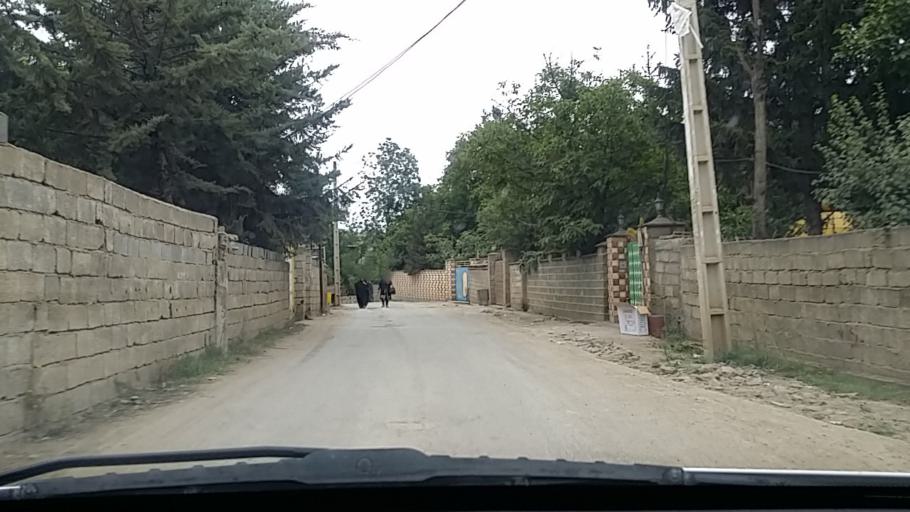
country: IR
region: Mazandaran
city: `Abbasabad
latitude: 36.5124
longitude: 51.1632
